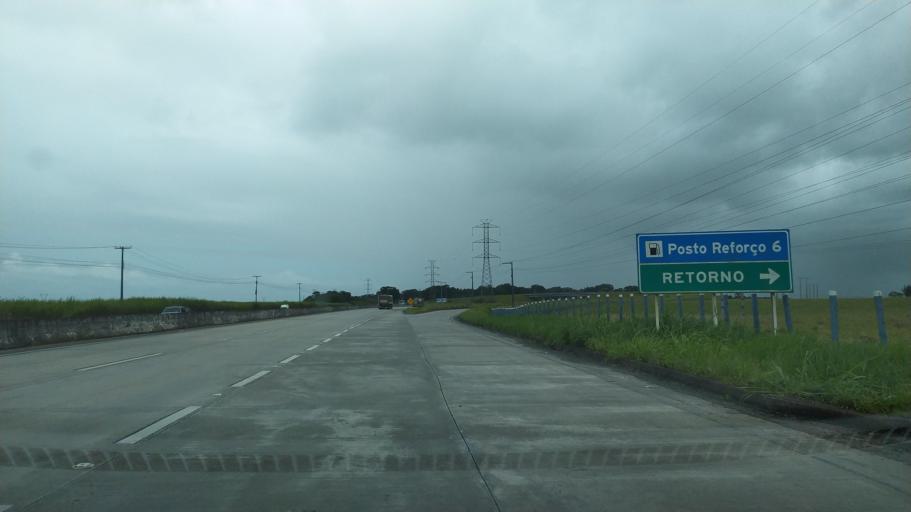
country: BR
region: Alagoas
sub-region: Rio Largo
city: Rio Largo
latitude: -9.4353
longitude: -35.8373
